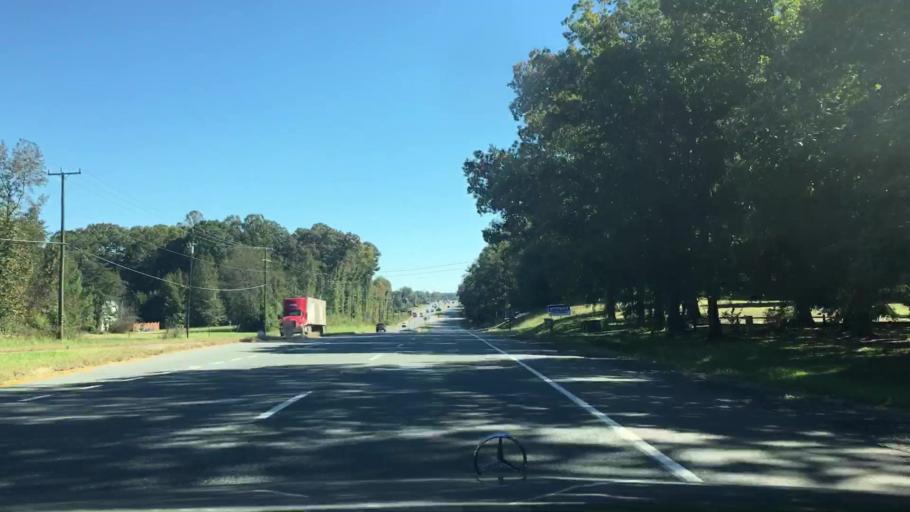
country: US
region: Virginia
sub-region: King George County
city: King George
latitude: 38.2796
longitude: -77.2184
